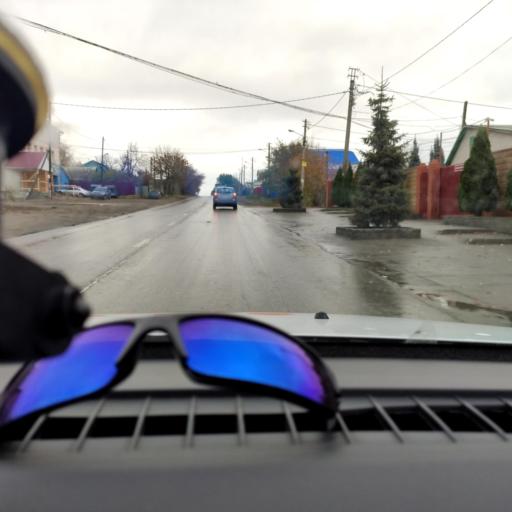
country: RU
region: Samara
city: Samara
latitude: 53.1765
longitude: 50.1826
